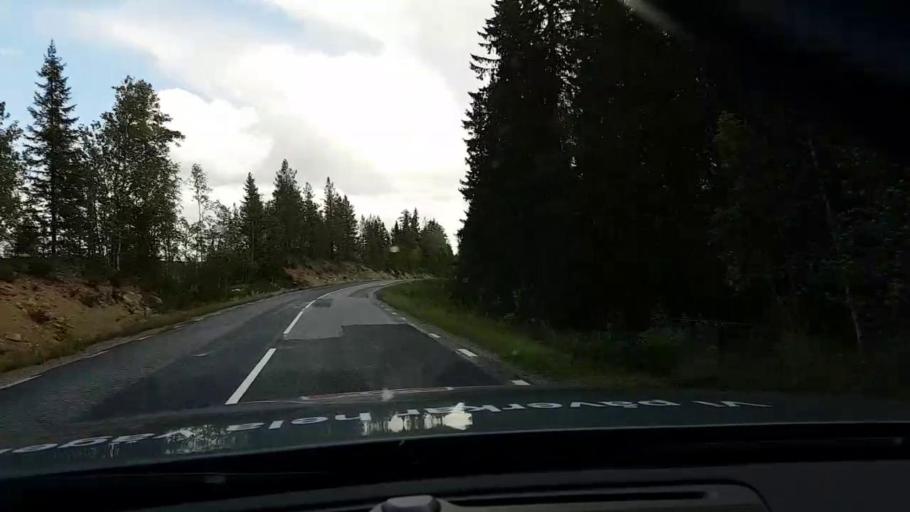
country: SE
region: Vaesterbotten
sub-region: Asele Kommun
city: Asele
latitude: 63.8340
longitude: 17.4467
